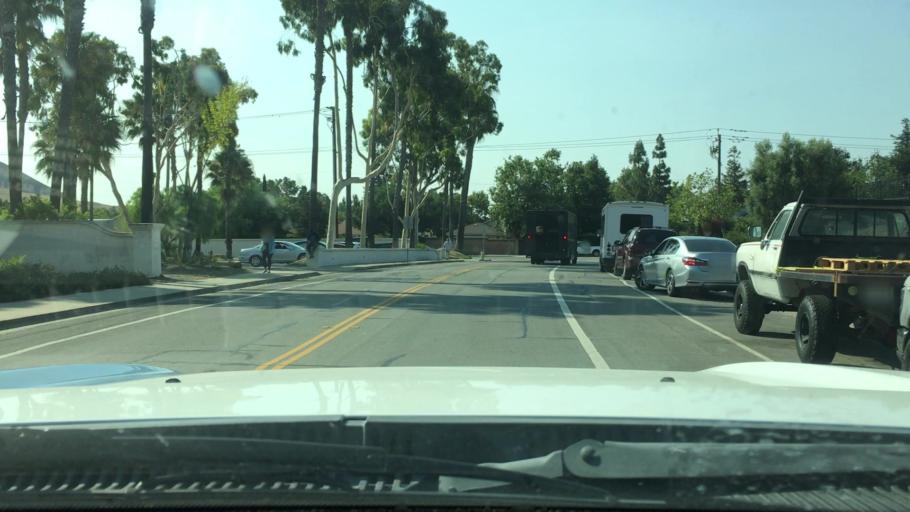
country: US
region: California
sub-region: San Luis Obispo County
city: San Luis Obispo
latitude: 35.2537
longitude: -120.6403
